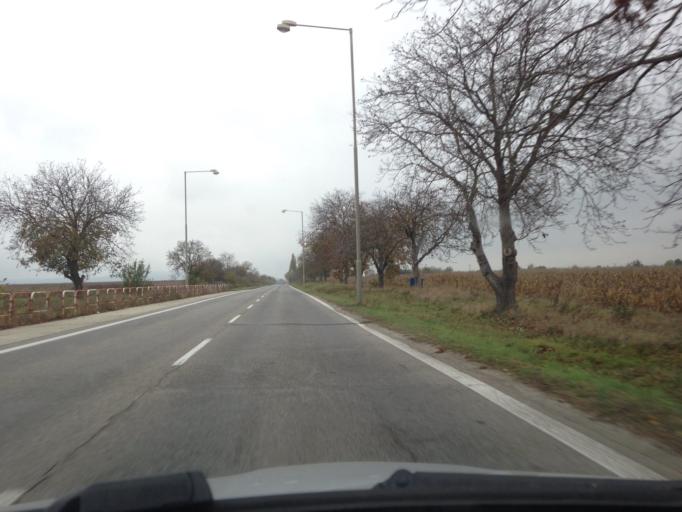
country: SK
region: Nitriansky
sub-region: Okres Nove Zamky
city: Sturovo
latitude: 47.7893
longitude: 18.6996
